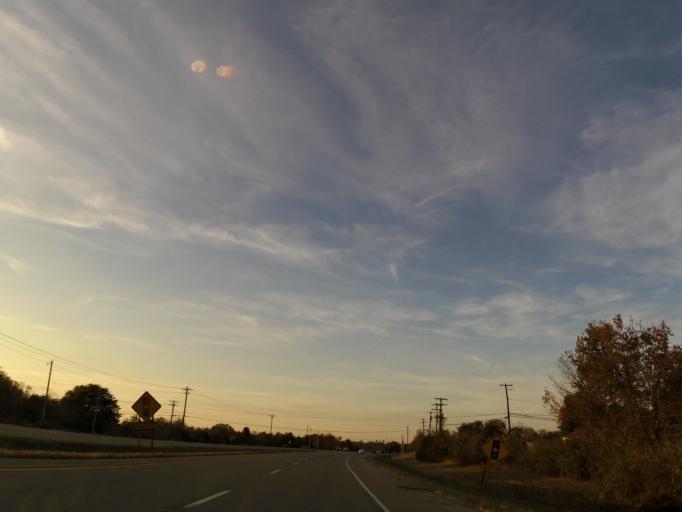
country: US
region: Kentucky
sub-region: Jessamine County
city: Nicholasville
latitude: 37.8617
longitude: -84.5929
